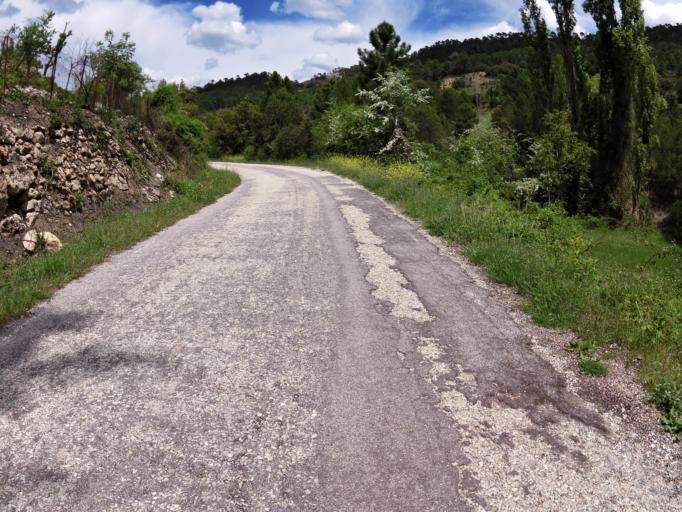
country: ES
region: Castille-La Mancha
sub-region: Provincia de Albacete
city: Paterna del Madera
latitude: 38.5772
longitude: -2.3384
